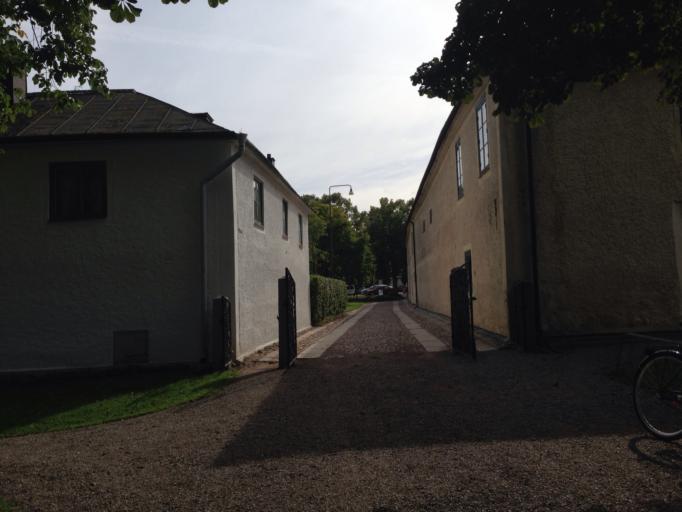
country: SE
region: OEstergoetland
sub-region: Vadstena Kommun
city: Vadstena
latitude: 58.4501
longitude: 14.8930
